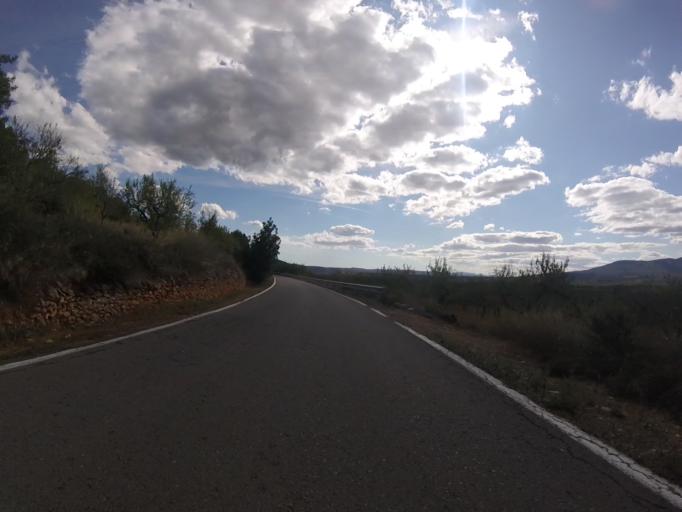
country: ES
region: Valencia
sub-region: Provincia de Castello
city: Cuevas de Vinroma
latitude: 40.3654
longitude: 0.1211
